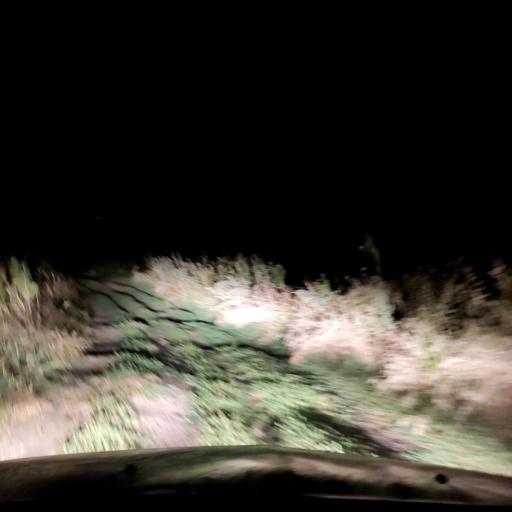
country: RU
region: Voronezj
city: Shilovo
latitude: 51.5938
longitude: 39.0278
